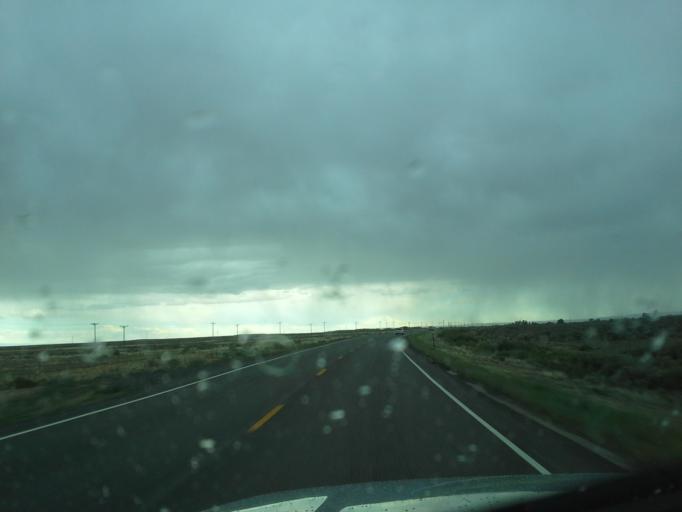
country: US
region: Wyoming
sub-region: Park County
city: Powell
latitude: 45.0247
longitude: -108.6329
